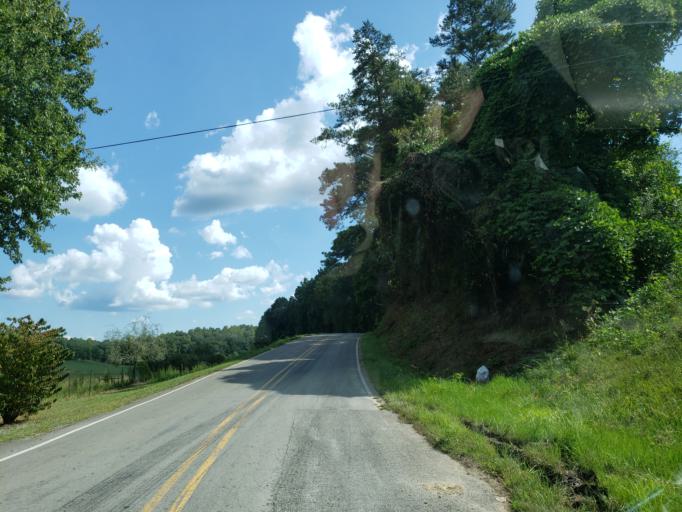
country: US
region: Georgia
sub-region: Pickens County
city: Jasper
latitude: 34.4195
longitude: -84.4573
